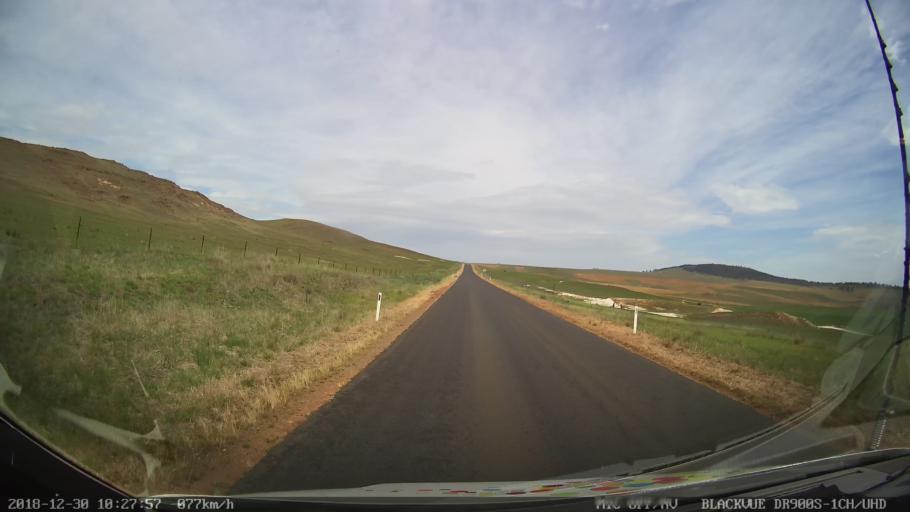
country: AU
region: New South Wales
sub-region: Snowy River
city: Berridale
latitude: -36.5089
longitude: 148.9278
